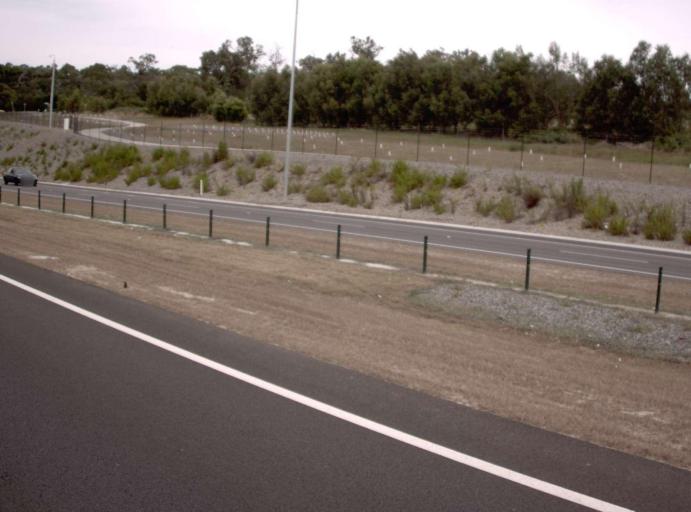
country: AU
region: Victoria
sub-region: Frankston
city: Langwarrin
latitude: -38.1752
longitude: 145.1622
